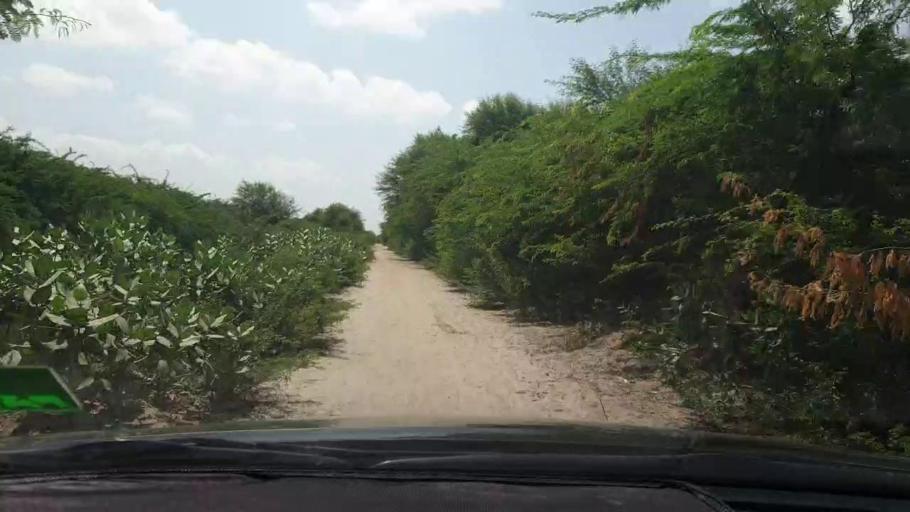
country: PK
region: Sindh
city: Tando Bago
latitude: 24.8704
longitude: 69.0711
